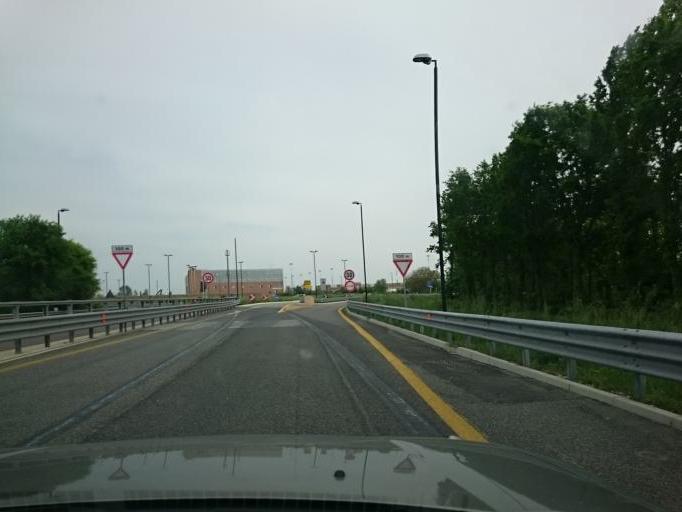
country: IT
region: Veneto
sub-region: Provincia di Venezia
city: Tessera
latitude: 45.5125
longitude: 12.3387
